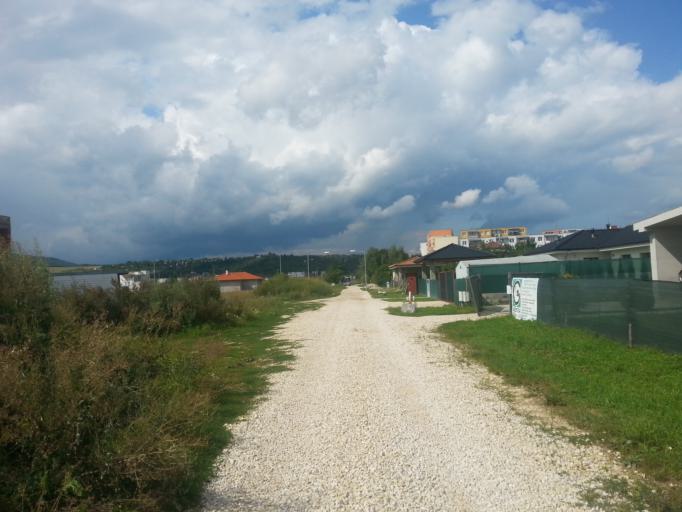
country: SK
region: Trenciansky
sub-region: Okres Nove Mesto nad Vahom
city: Nove Mesto nad Vahom
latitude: 48.7491
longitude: 17.8211
